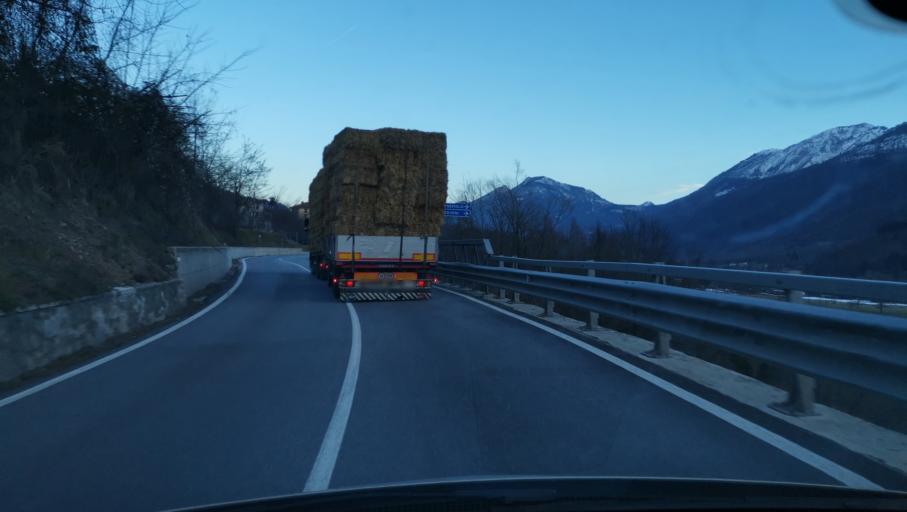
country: IT
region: Piedmont
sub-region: Provincia di Cuneo
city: Demonte
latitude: 44.3132
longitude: 7.2861
